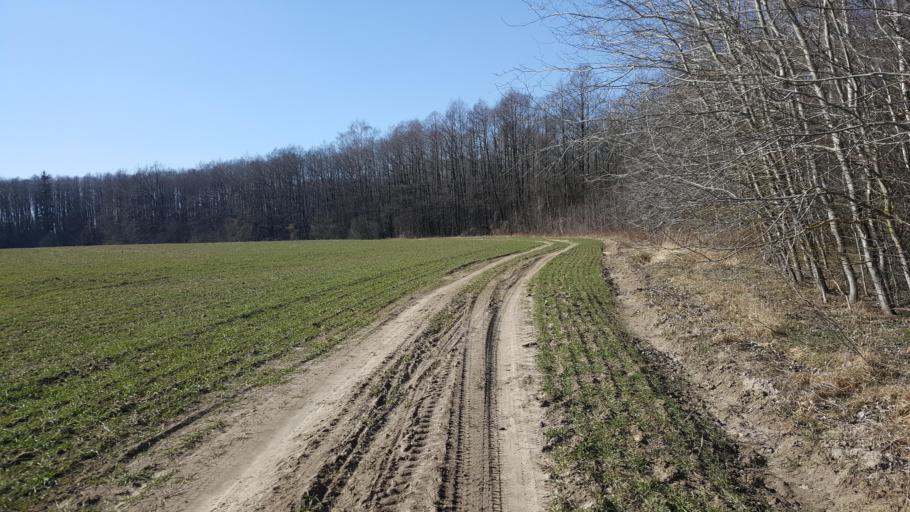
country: BY
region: Brest
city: Kamyanyets
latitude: 52.3664
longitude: 23.7673
